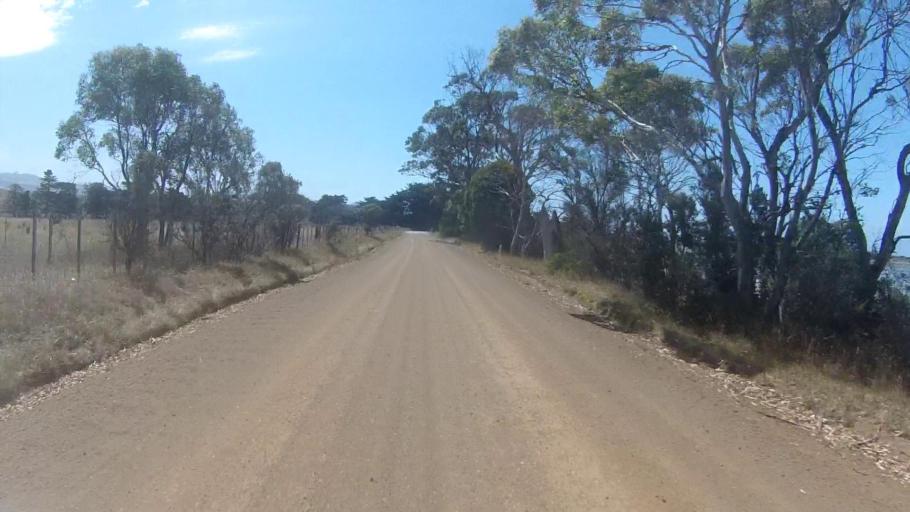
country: AU
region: Tasmania
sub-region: Sorell
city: Sorell
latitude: -42.8315
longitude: 147.8563
